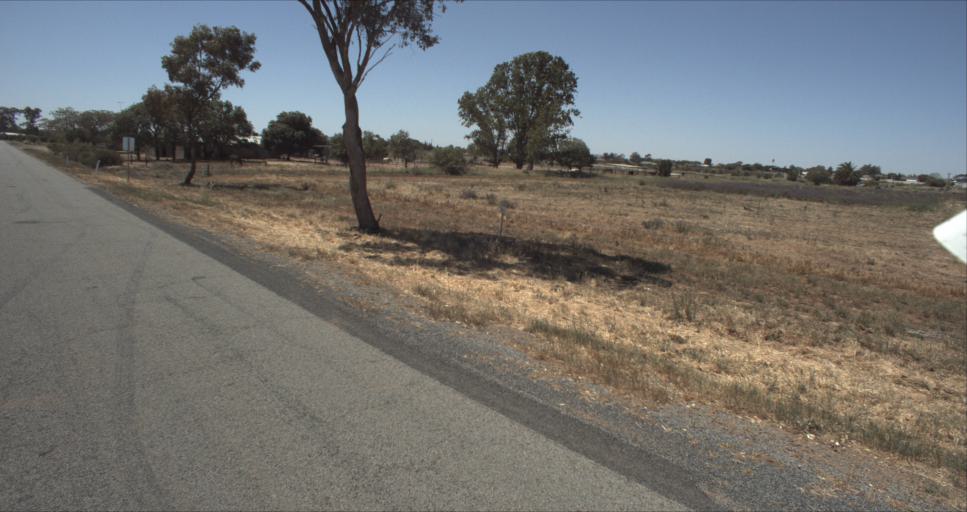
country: AU
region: New South Wales
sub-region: Leeton
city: Leeton
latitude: -34.5362
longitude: 146.3968
